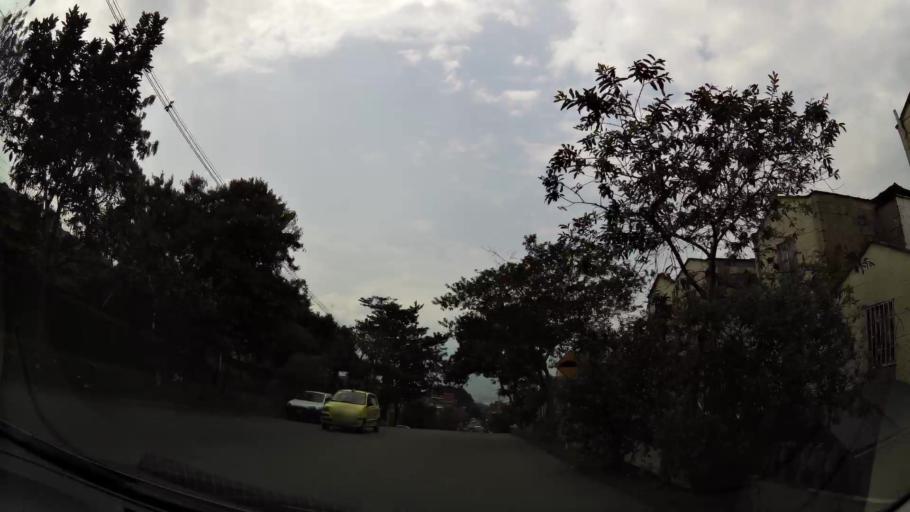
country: CO
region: Antioquia
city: Medellin
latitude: 6.2317
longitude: -75.5518
